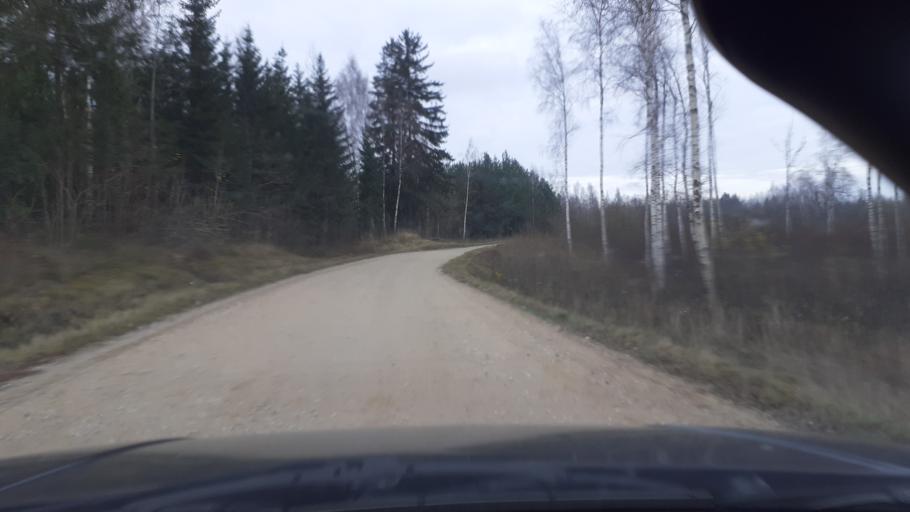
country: LV
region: Alsunga
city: Alsunga
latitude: 56.9445
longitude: 21.6365
